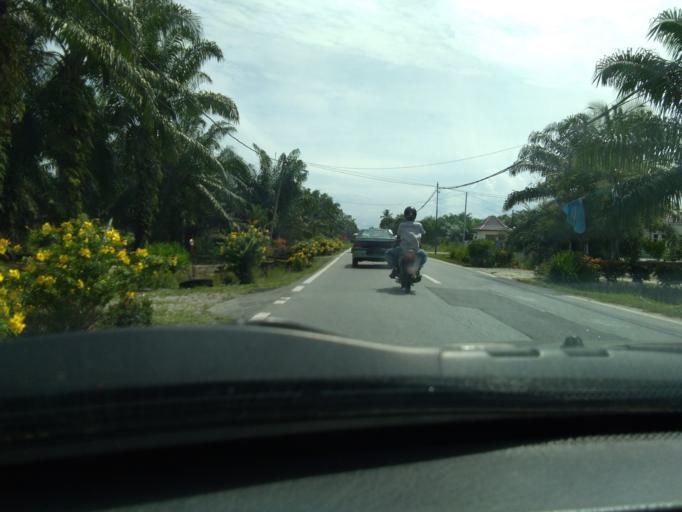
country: MY
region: Perak
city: Bagan Serai
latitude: 5.0300
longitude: 100.5597
